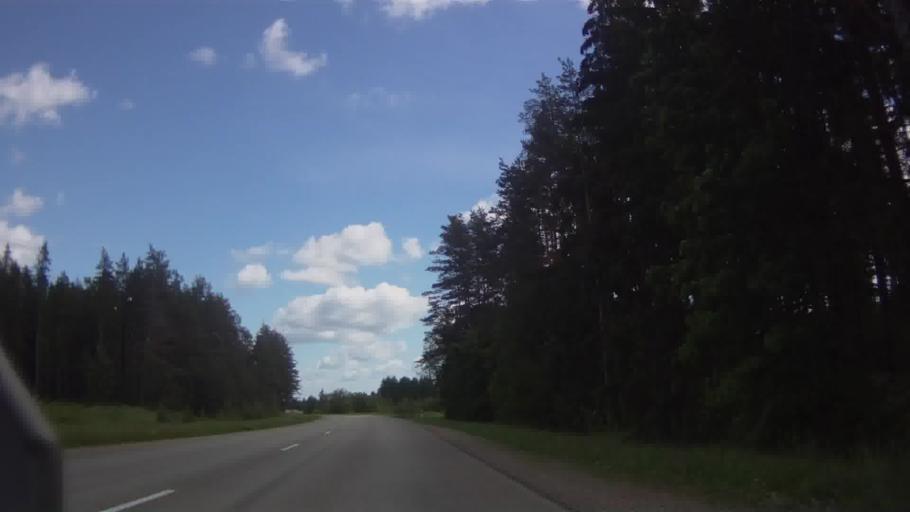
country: LV
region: Varaklani
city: Varaklani
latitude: 56.5871
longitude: 26.7058
